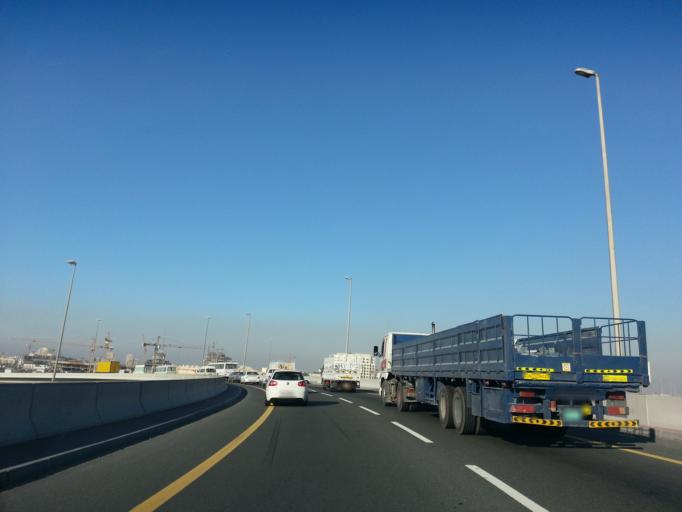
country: AE
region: Dubai
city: Dubai
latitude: 25.0422
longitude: 55.2019
